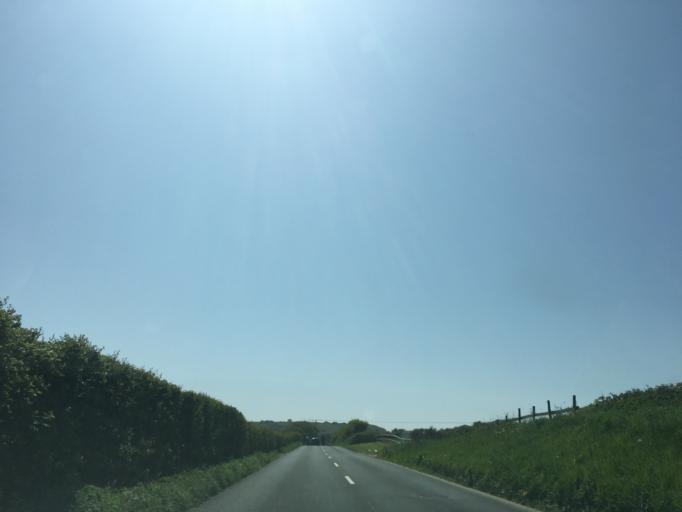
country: GB
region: England
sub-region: Isle of Wight
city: Niton
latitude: 50.5933
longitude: -1.2754
